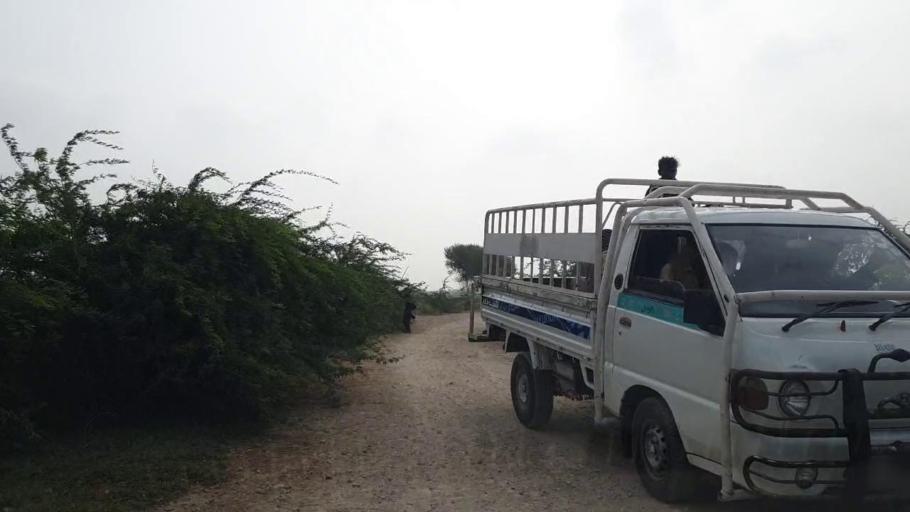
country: PK
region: Sindh
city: Kario
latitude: 24.8570
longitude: 68.5256
